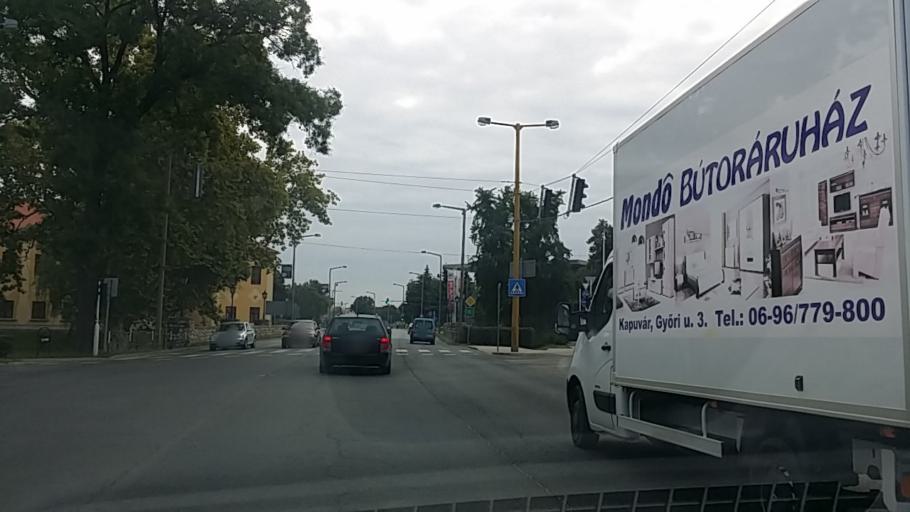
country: HU
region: Gyor-Moson-Sopron
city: Kapuvar
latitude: 47.5934
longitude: 17.0255
